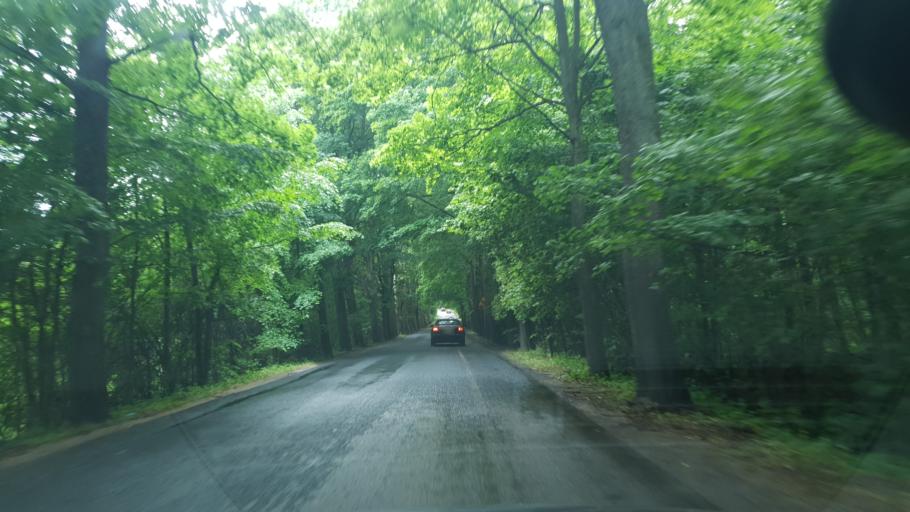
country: PL
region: Pomeranian Voivodeship
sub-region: Powiat kartuski
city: Chmielno
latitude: 54.2648
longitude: 18.0473
